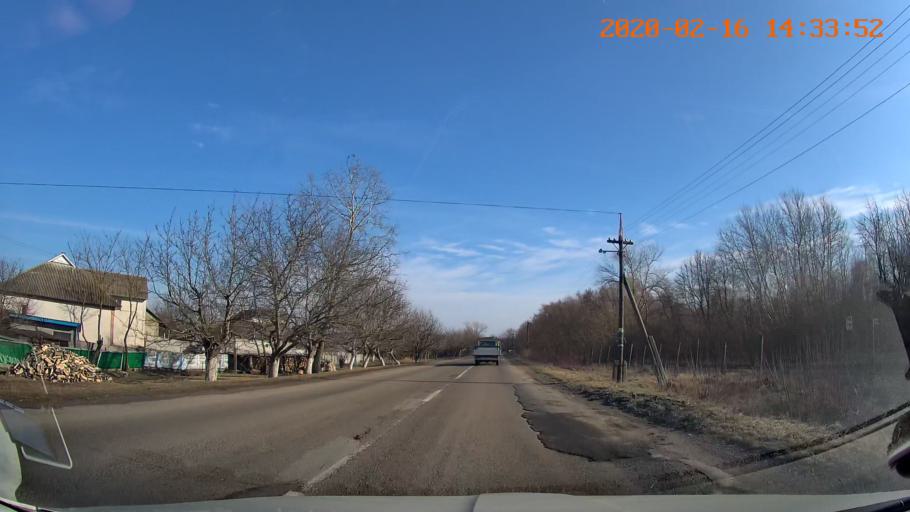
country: RO
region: Botosani
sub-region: Comuna Hudesti
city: Alba
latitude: 48.2218
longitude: 26.4700
